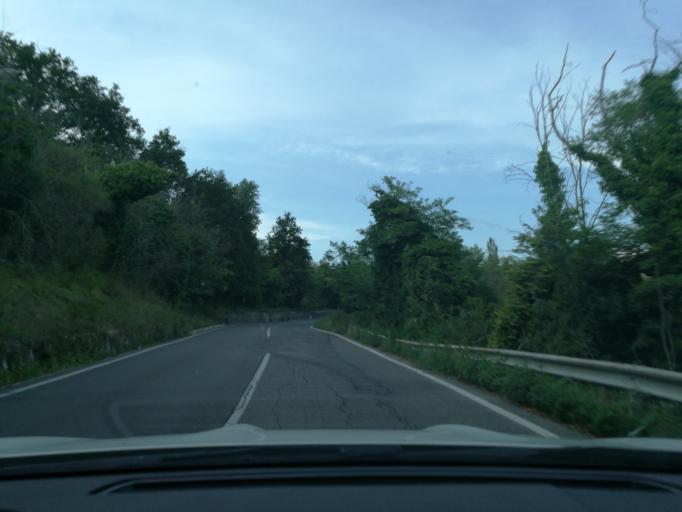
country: IT
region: Umbria
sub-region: Provincia di Terni
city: San Gemini
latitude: 42.6281
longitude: 12.5520
